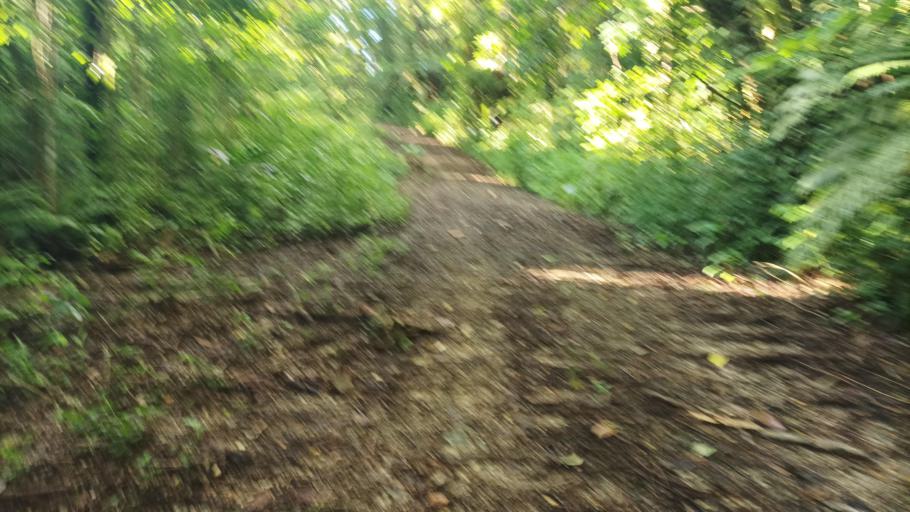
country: FM
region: Pohnpei
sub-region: Kolonia Municipality
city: Kolonia Town
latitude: 6.9658
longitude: 158.1868
